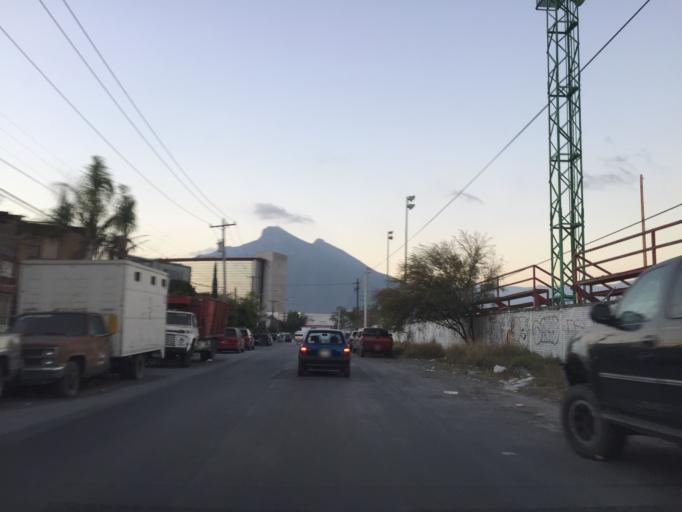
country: MX
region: Nuevo Leon
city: Guadalupe
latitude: 25.6970
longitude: -100.2236
